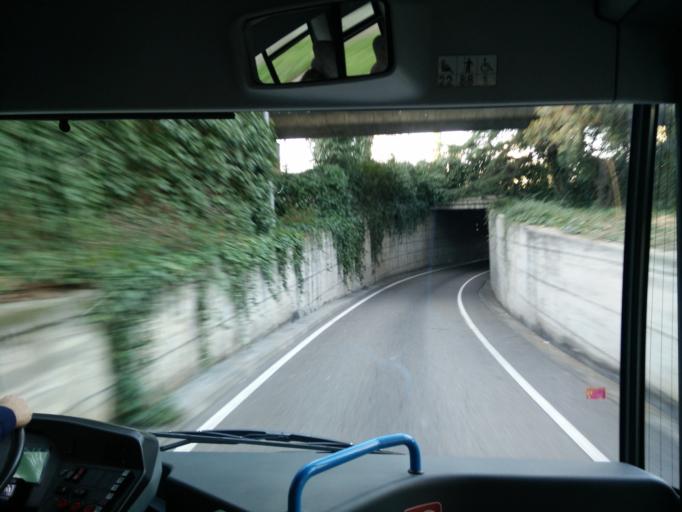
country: ES
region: Madrid
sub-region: Provincia de Madrid
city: Barajas de Madrid
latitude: 40.4666
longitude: -3.5703
